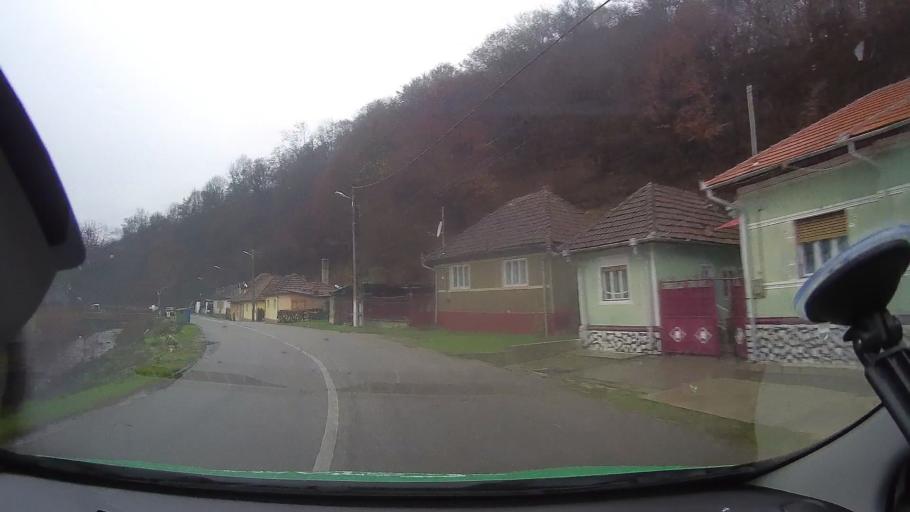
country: RO
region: Arad
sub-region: Comuna Moneasa
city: Moneasa
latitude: 46.4563
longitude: 22.2490
